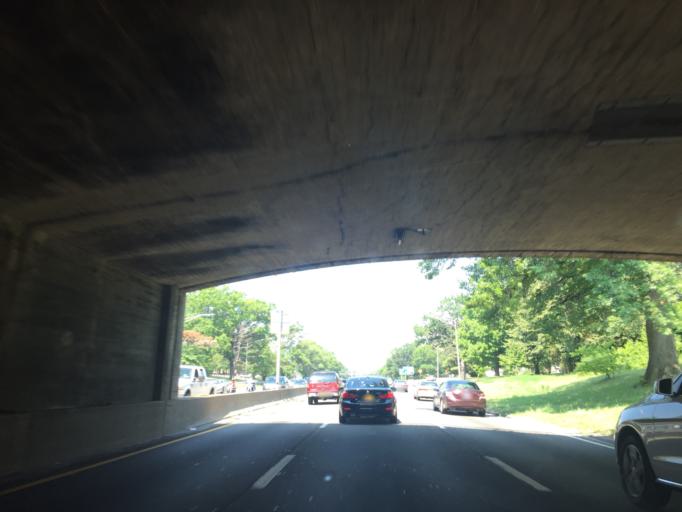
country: US
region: New York
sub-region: Nassau County
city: South Valley Stream
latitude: 40.6660
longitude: -73.7579
